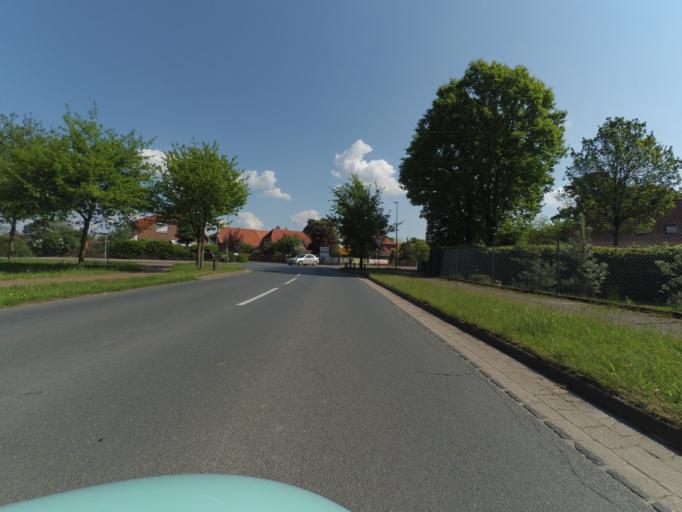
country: DE
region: Lower Saxony
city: Isernhagen Farster Bauerschaft
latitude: 52.4933
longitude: 9.9003
